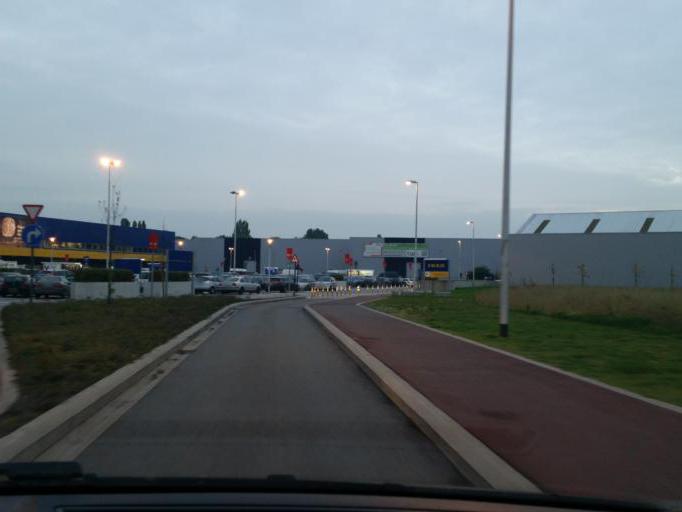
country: BE
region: Flanders
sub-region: Provincie Antwerpen
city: Aartselaar
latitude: 51.1580
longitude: 4.3851
